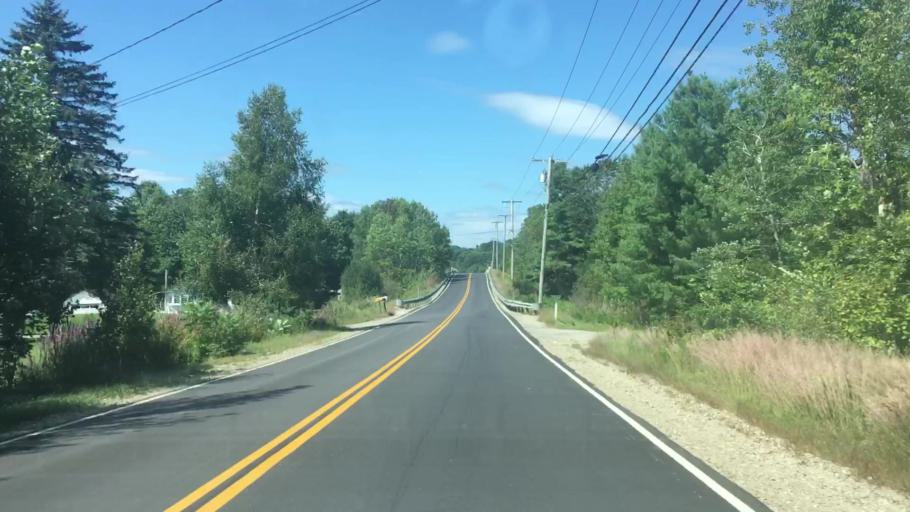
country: US
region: Maine
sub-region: Androscoggin County
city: Sabattus
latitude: 44.0774
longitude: -70.1197
